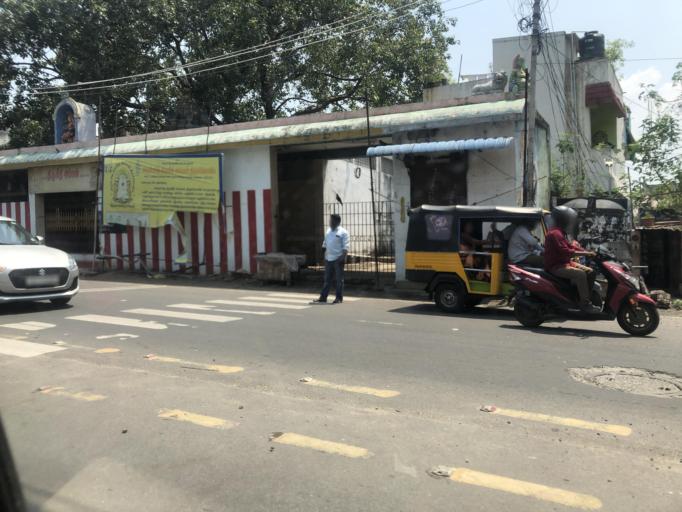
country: IN
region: Tamil Nadu
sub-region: Chennai
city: Gandhi Nagar
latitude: 12.9808
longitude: 80.2594
